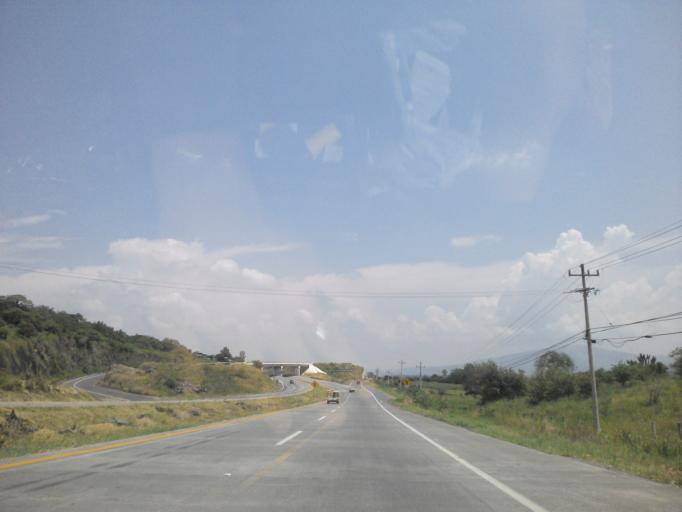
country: MX
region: Jalisco
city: Puente Grande
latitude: 20.5739
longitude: -103.1710
